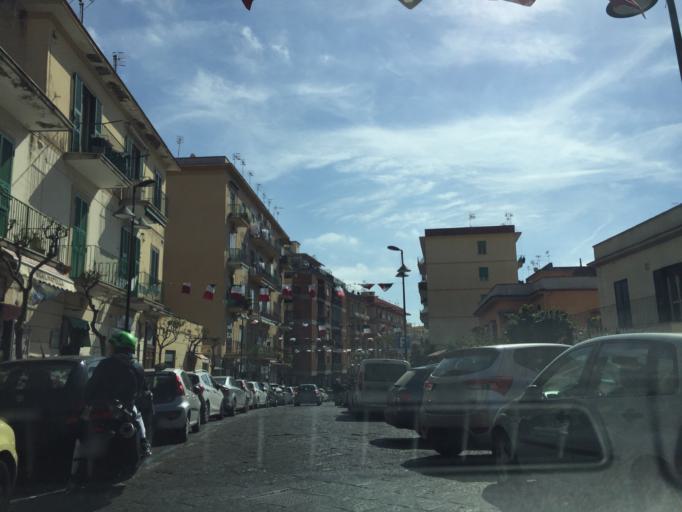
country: IT
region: Campania
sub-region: Provincia di Napoli
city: Ercolano
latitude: 40.8106
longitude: 14.3527
